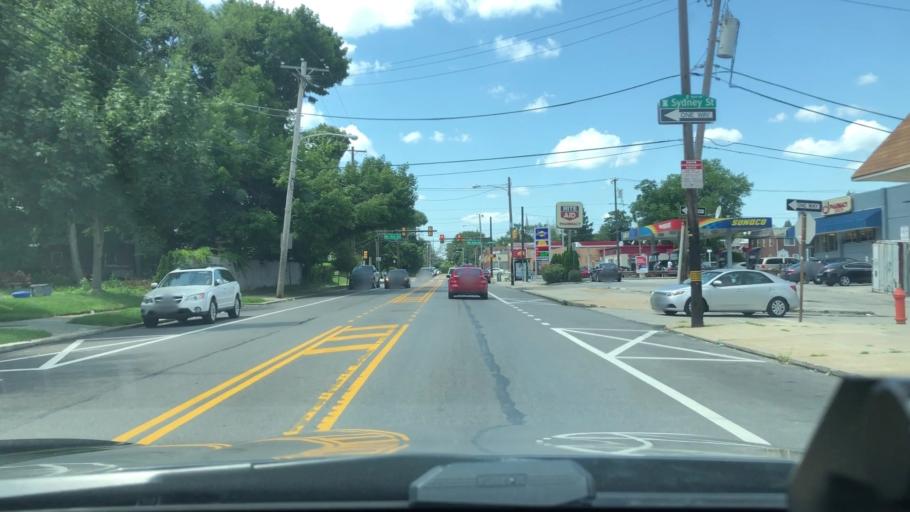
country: US
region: Pennsylvania
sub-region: Montgomery County
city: Wyndmoor
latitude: 40.0682
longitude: -75.1804
